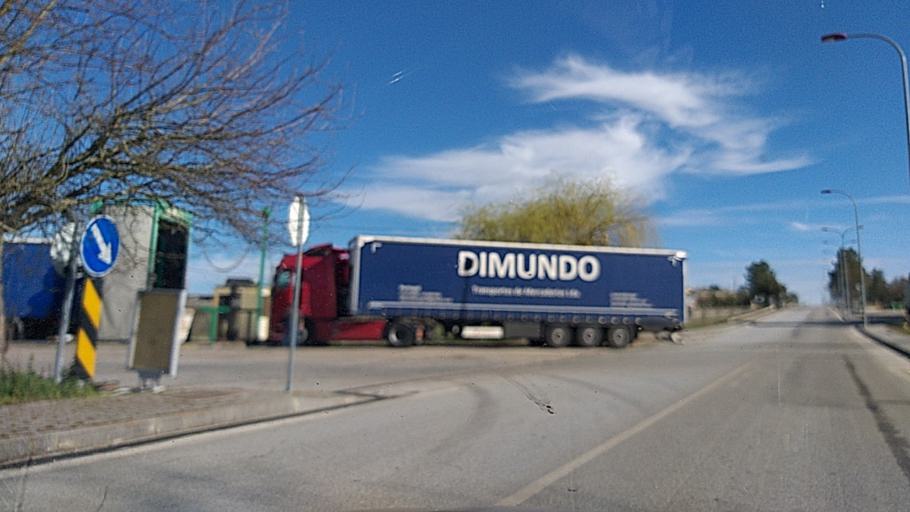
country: ES
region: Castille and Leon
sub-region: Provincia de Salamanca
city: Fuentes de Onoro
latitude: 40.5998
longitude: -6.9981
